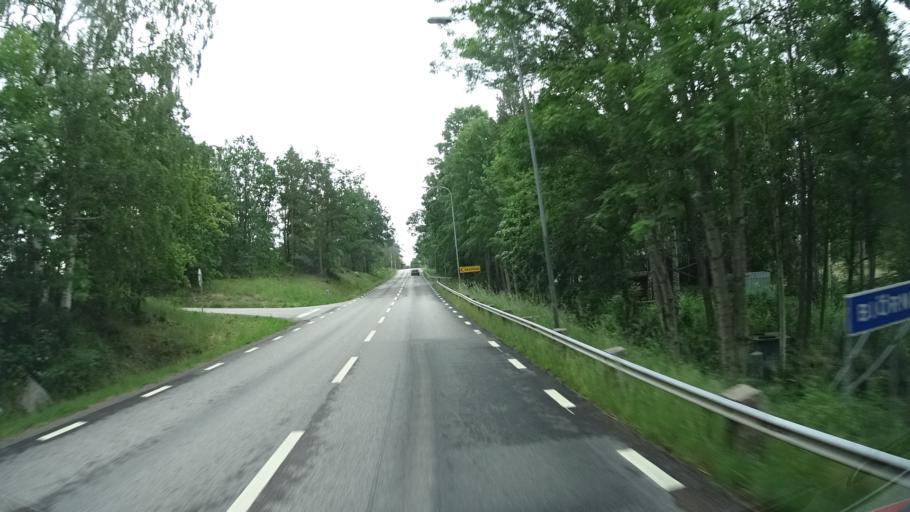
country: SE
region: Kalmar
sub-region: Oskarshamns Kommun
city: Oskarshamn
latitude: 57.3172
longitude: 16.2743
